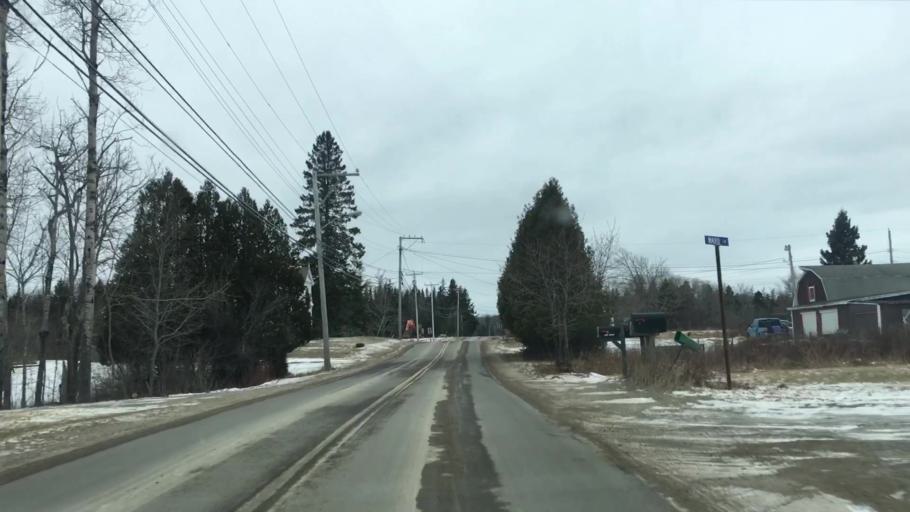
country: US
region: Maine
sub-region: Washington County
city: Machiasport
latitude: 44.7052
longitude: -67.4008
